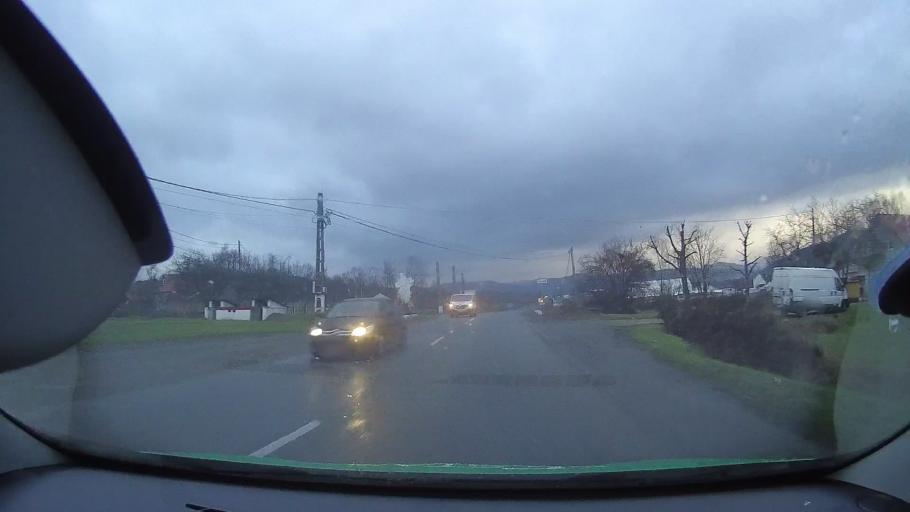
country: RO
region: Hunedoara
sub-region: Municipiul Brad
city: Brad
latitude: 46.1546
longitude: 22.7648
